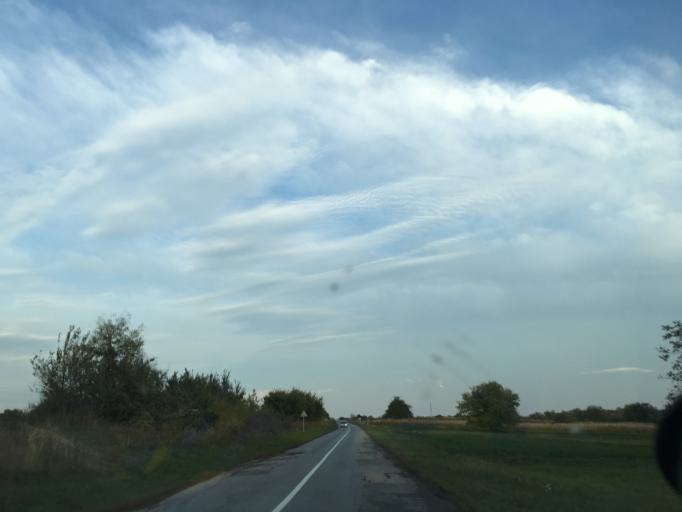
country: RS
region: Autonomna Pokrajina Vojvodina
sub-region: Juznobanatski Okrug
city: Kovin
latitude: 44.8499
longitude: 21.0131
